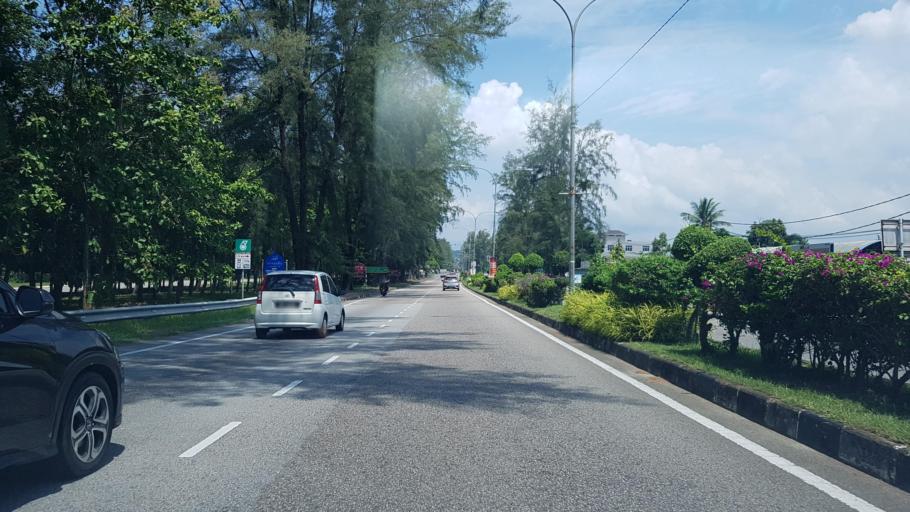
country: MY
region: Terengganu
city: Kuala Terengganu
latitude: 5.2893
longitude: 103.1687
